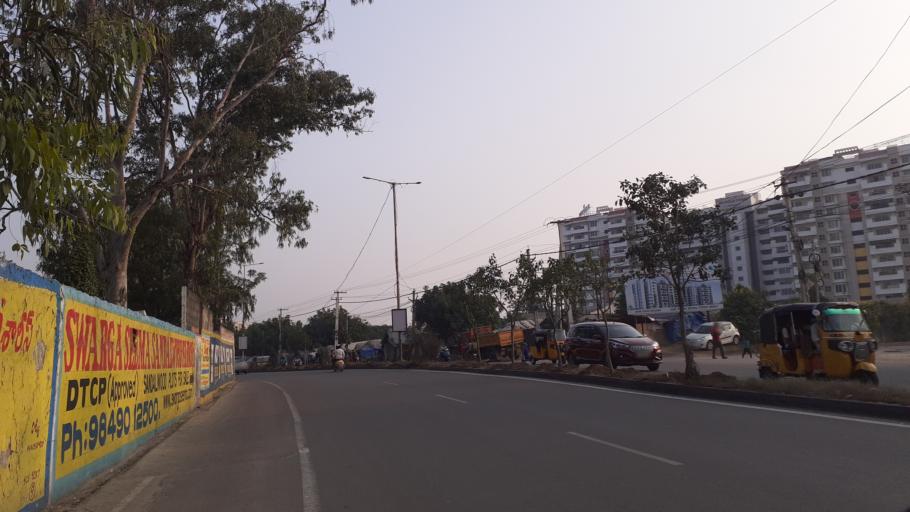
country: IN
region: Telangana
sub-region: Medak
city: Serilingampalle
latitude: 17.4896
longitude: 78.3542
